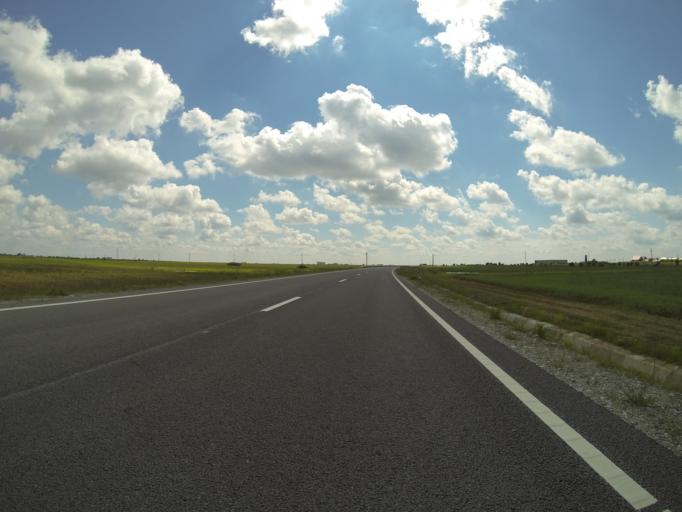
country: RO
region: Dolj
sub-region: Comuna Carcea
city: Carcea
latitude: 44.2654
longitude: 23.9106
